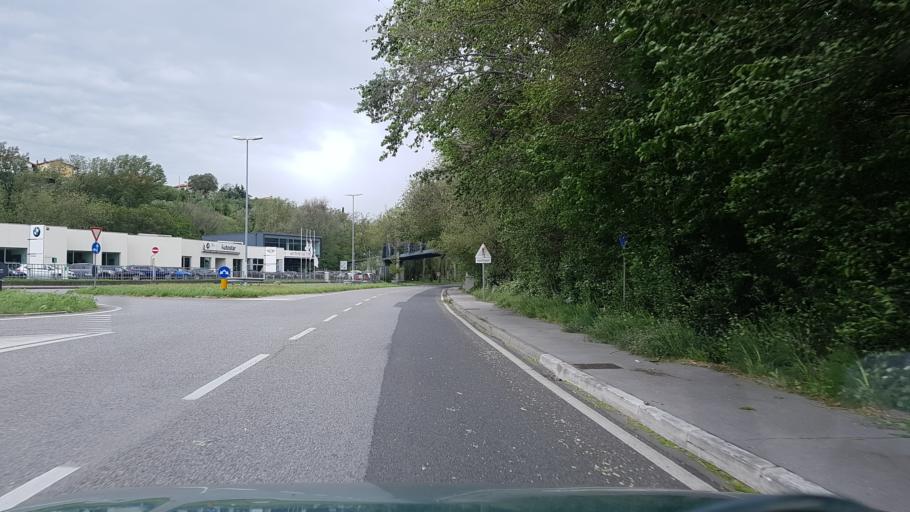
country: IT
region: Friuli Venezia Giulia
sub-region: Provincia di Trieste
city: Domio
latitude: 45.6092
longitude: 13.8153
